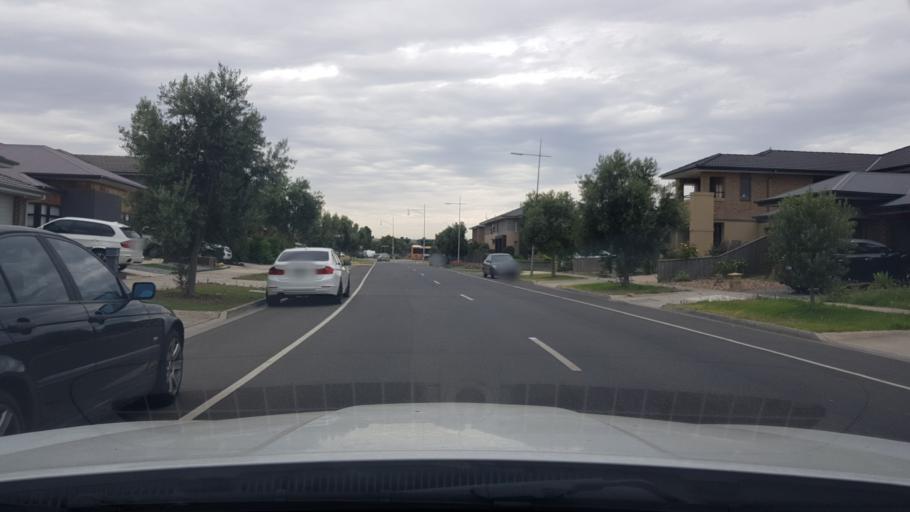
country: AU
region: Victoria
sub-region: Whittlesea
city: Lalor
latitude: -37.6649
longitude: 144.9963
